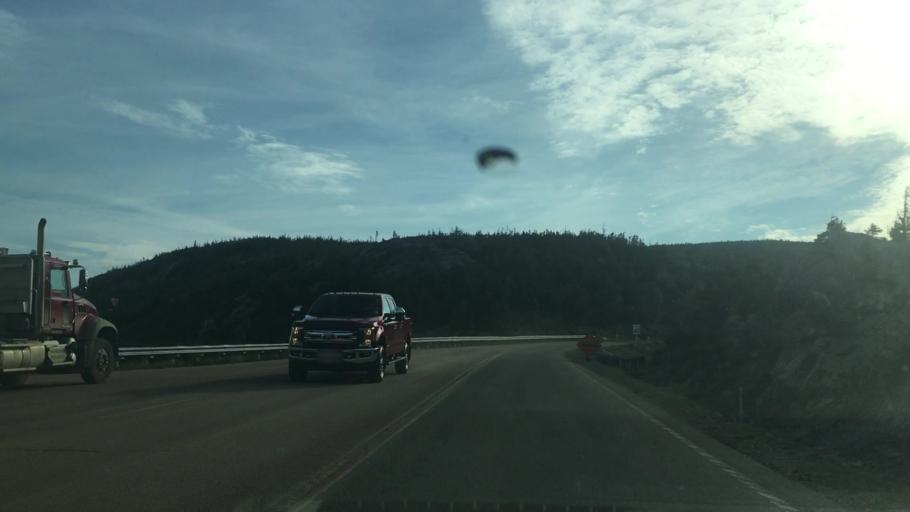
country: CA
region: Nova Scotia
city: Sydney Mines
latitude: 46.8177
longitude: -60.8337
